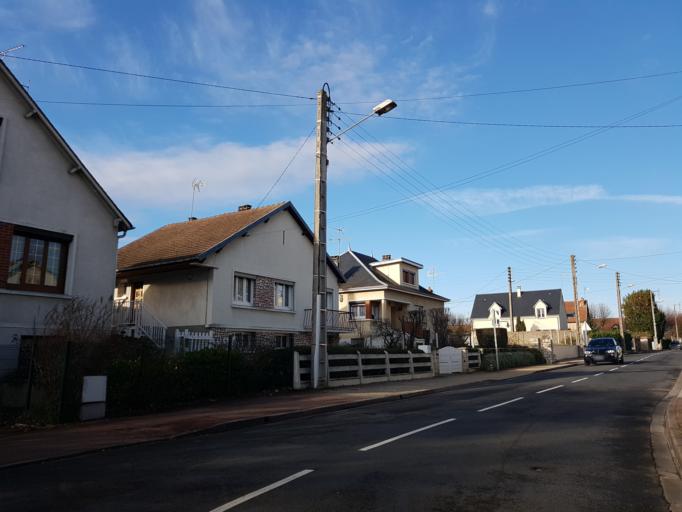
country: FR
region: Centre
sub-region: Departement du Loiret
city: Saint-Jean-le-Blanc
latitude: 47.8854
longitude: 1.9241
